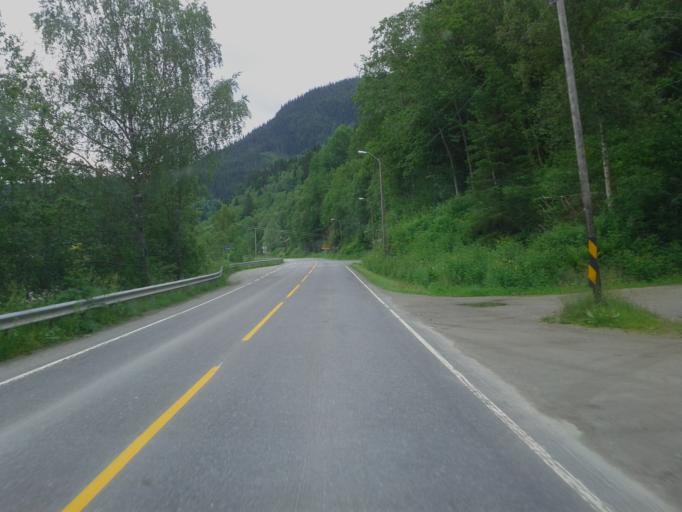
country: NO
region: Sor-Trondelag
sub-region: Midtre Gauldal
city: Storen
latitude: 63.0049
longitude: 10.4546
